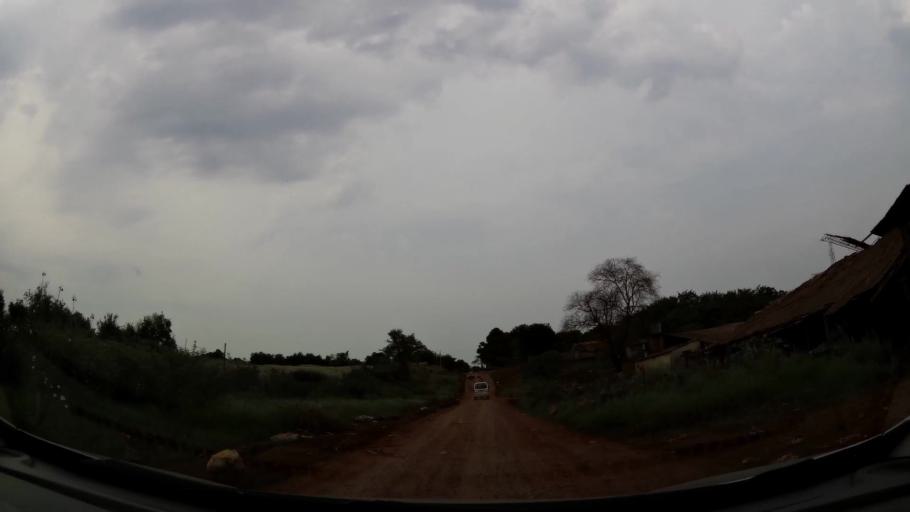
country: PY
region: Alto Parana
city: Presidente Franco
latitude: -25.5447
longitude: -54.6530
